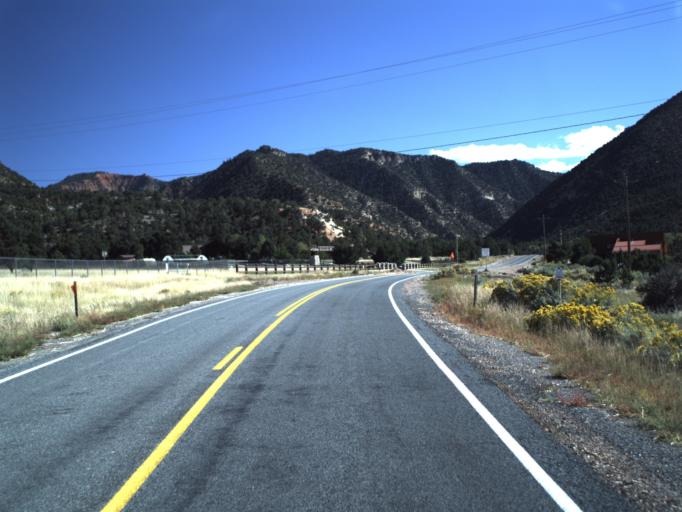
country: US
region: Utah
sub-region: Iron County
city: Parowan
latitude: 37.8324
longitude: -112.8158
